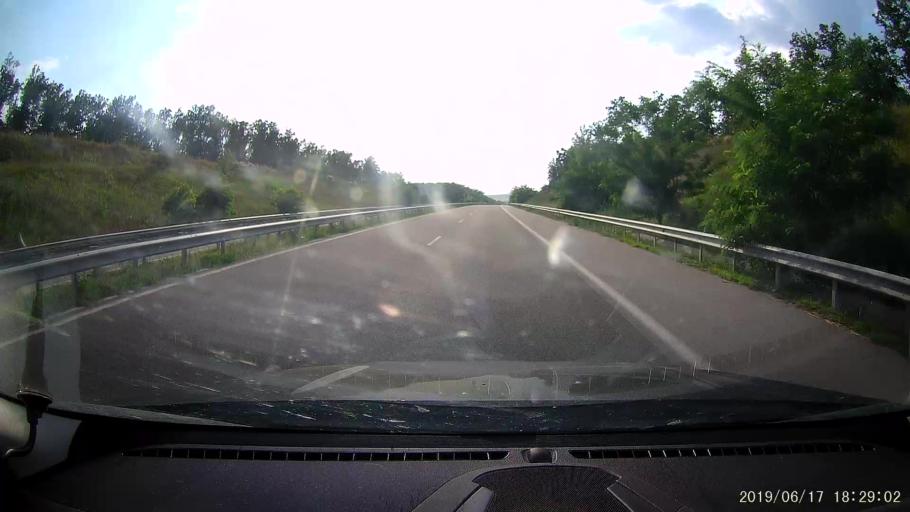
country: BG
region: Khaskovo
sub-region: Obshtina Dimitrovgrad
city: Dimitrovgrad
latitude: 42.0260
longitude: 25.5649
